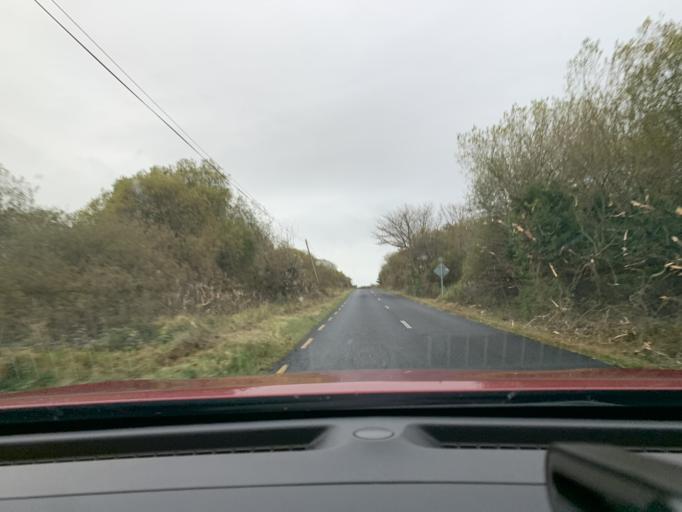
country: IE
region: Connaught
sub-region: Roscommon
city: Ballaghaderreen
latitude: 53.9536
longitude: -8.5440
